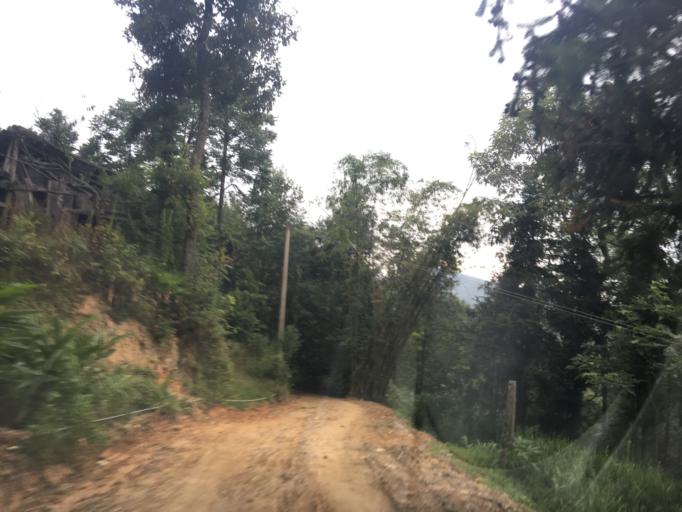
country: CN
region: Guangxi Zhuangzu Zizhiqu
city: Xinzhou
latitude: 25.1670
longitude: 105.6853
